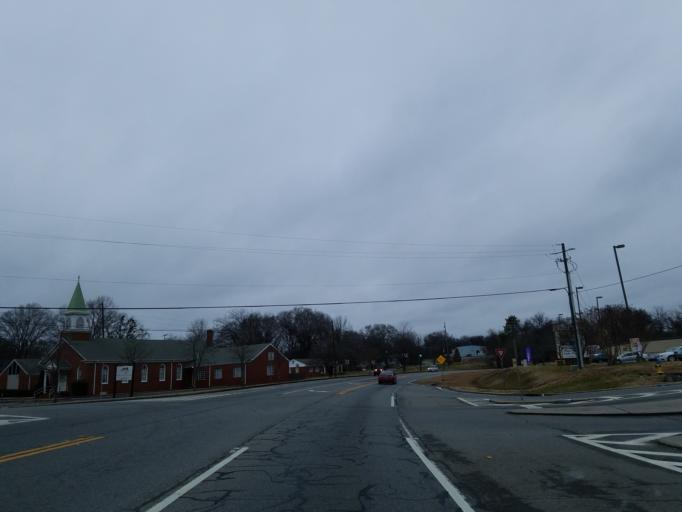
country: US
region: Georgia
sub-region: Bartow County
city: Cartersville
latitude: 34.1803
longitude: -84.8153
